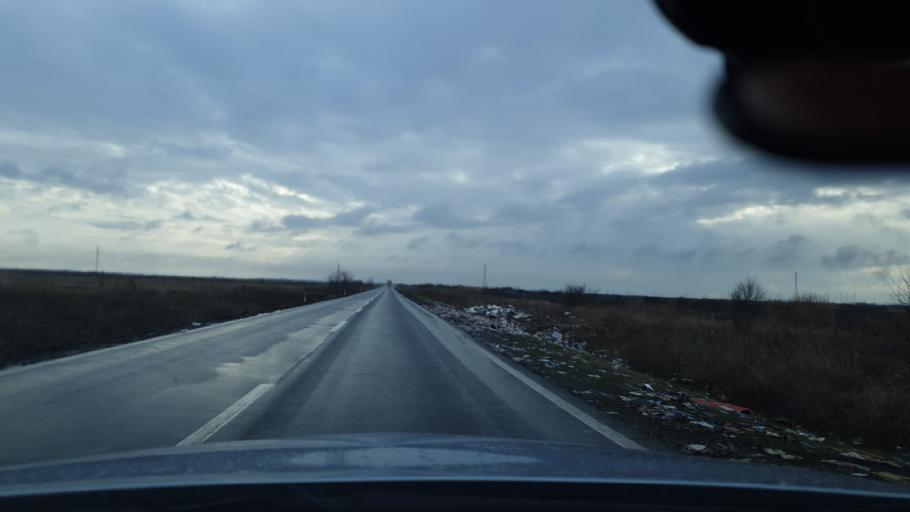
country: RS
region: Autonomna Pokrajina Vojvodina
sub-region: Juznobanatski Okrug
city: Kovin
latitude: 44.8011
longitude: 20.9022
